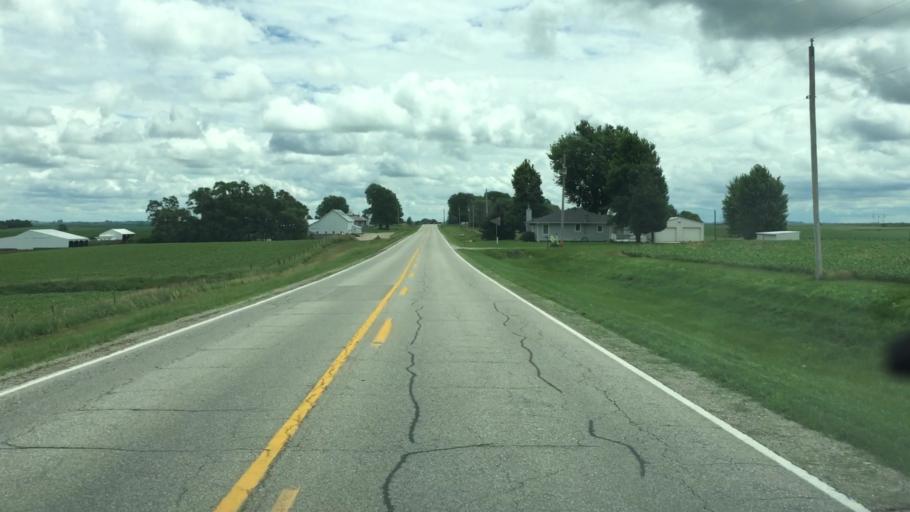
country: US
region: Iowa
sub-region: Jasper County
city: Monroe
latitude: 41.5735
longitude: -93.0935
